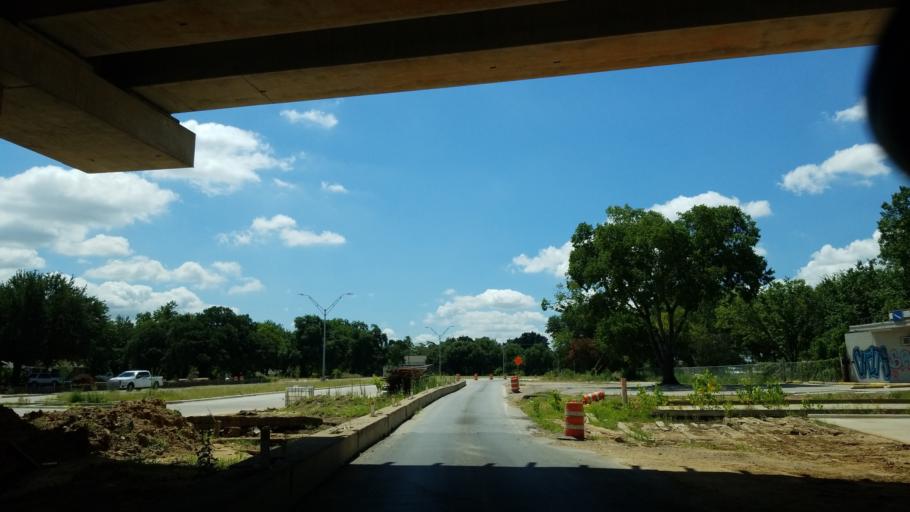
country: US
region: Texas
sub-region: Dallas County
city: Dallas
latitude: 32.7457
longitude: -96.7588
